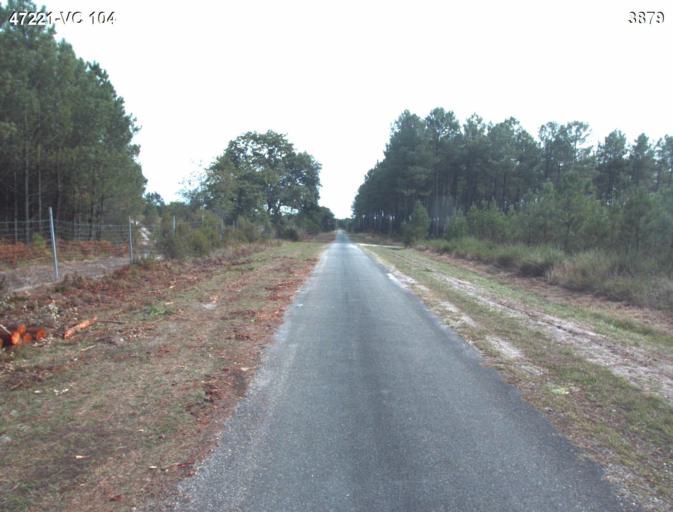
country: FR
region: Aquitaine
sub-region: Departement du Lot-et-Garonne
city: Mezin
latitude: 44.1263
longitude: 0.1813
